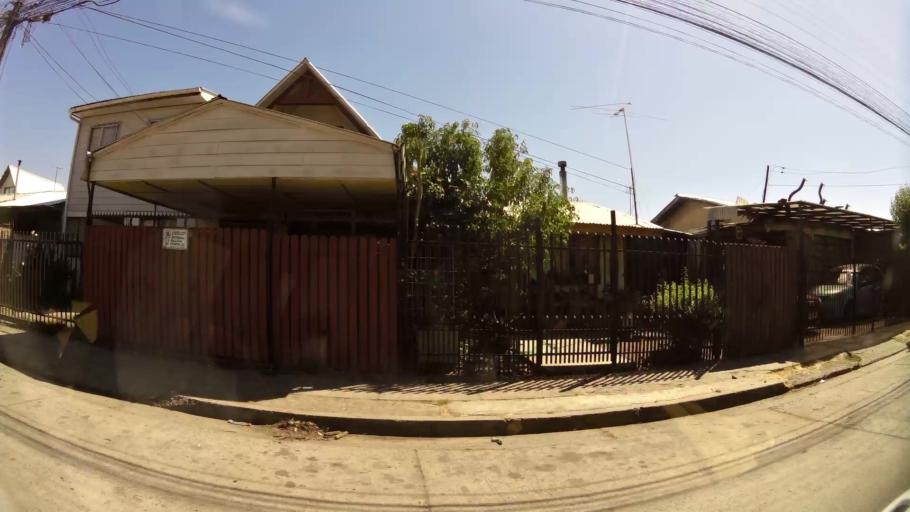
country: CL
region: Maule
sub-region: Provincia de Curico
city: Curico
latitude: -34.9661
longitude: -71.2398
